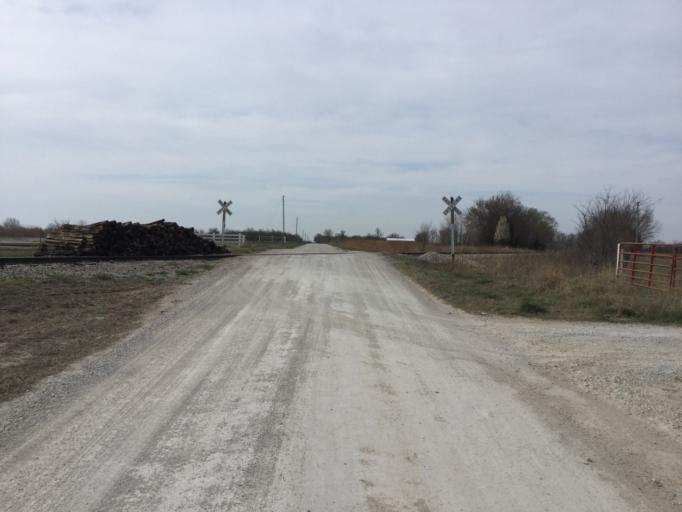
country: US
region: Kansas
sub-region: Wilson County
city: Fredonia
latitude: 37.5097
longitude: -95.8517
